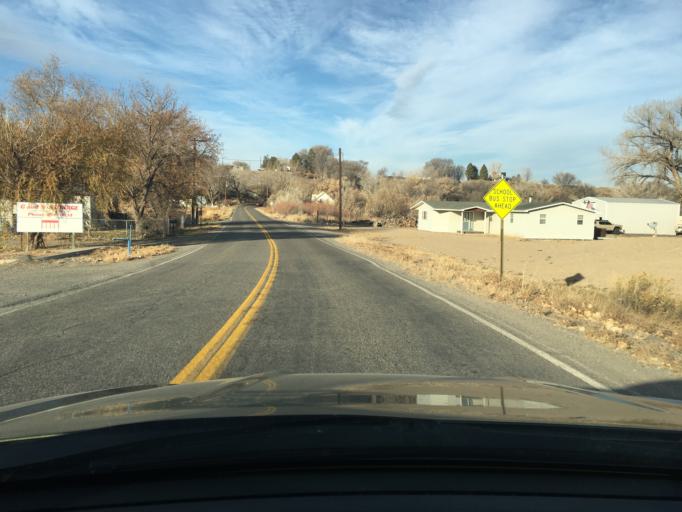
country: US
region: Colorado
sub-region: Delta County
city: Delta
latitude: 38.7409
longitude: -108.0828
